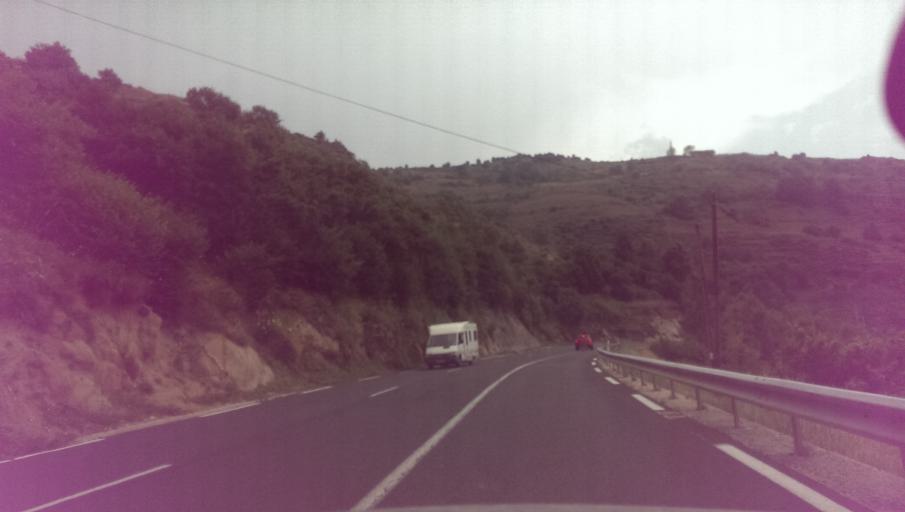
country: ES
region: Catalonia
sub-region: Provincia de Girona
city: Llivia
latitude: 42.5067
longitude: 2.1357
